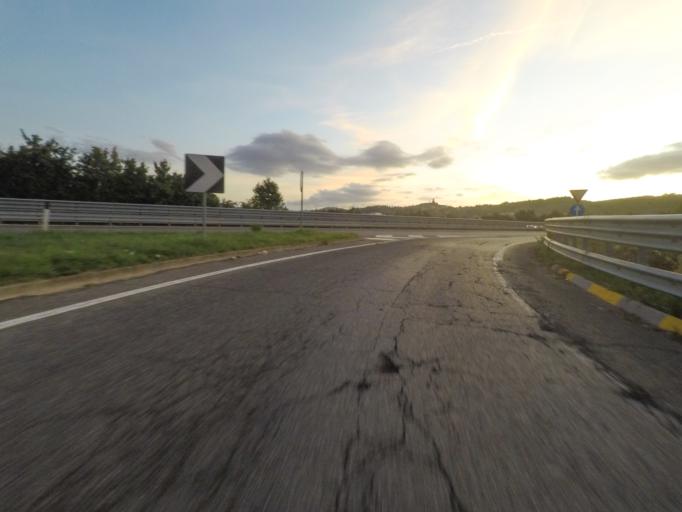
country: IT
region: Tuscany
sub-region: Provincia di Siena
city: Sinalunga
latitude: 43.2228
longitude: 11.7548
